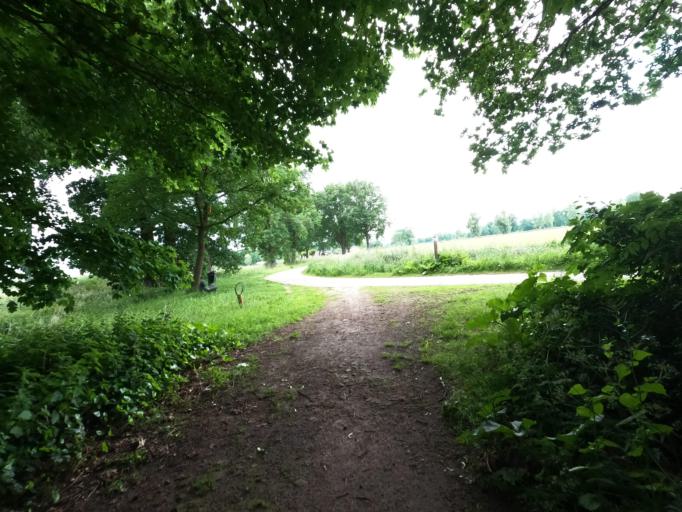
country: BE
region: Flanders
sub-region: Provincie Antwerpen
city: Kalmthout
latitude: 51.3970
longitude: 4.4815
